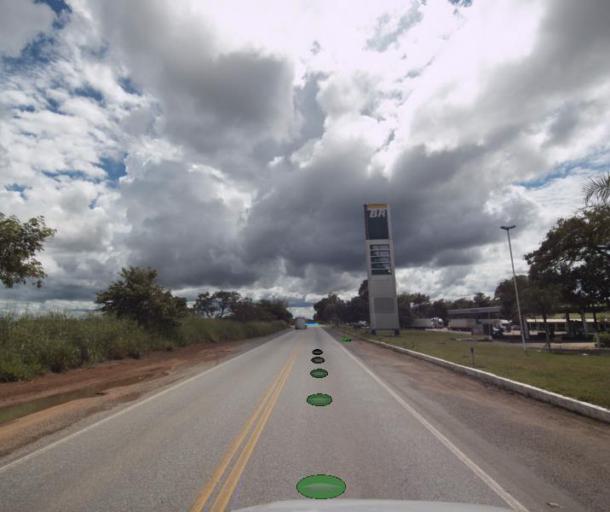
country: BR
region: Goias
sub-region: Uruacu
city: Uruacu
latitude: -14.2823
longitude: -49.1486
